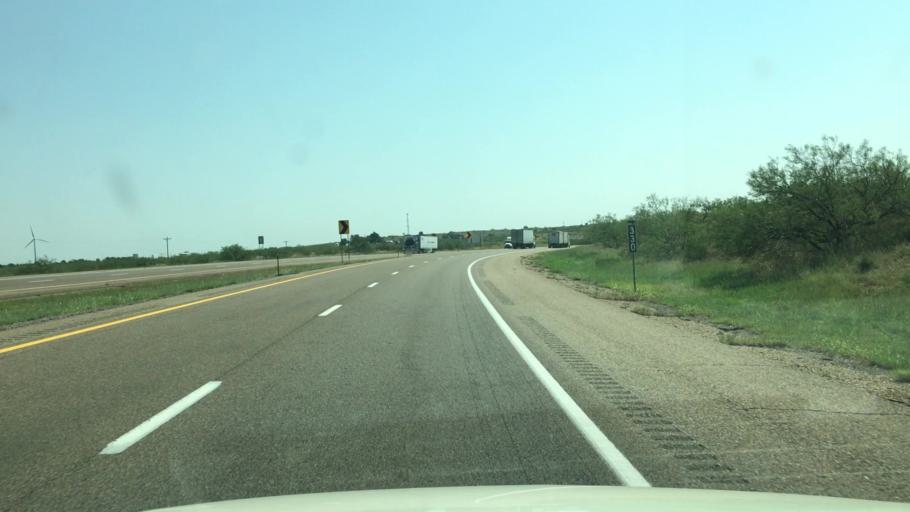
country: US
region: New Mexico
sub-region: Quay County
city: Tucumcari
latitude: 35.1566
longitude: -103.7644
